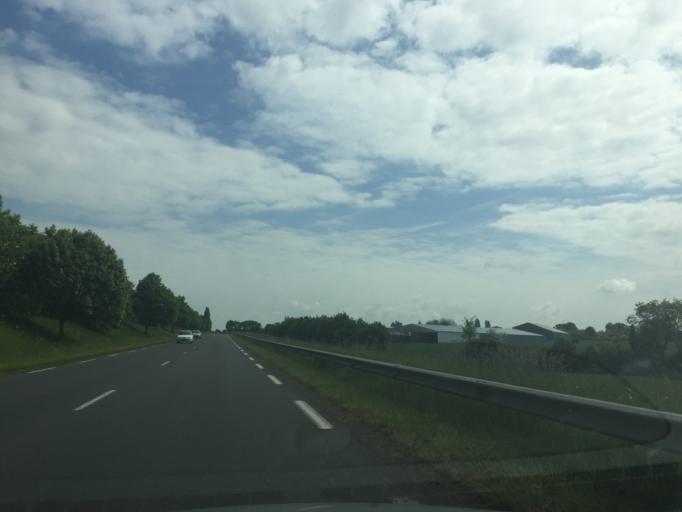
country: FR
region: Poitou-Charentes
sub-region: Departement de la Vienne
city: Lusignan
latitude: 46.4306
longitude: 0.1314
